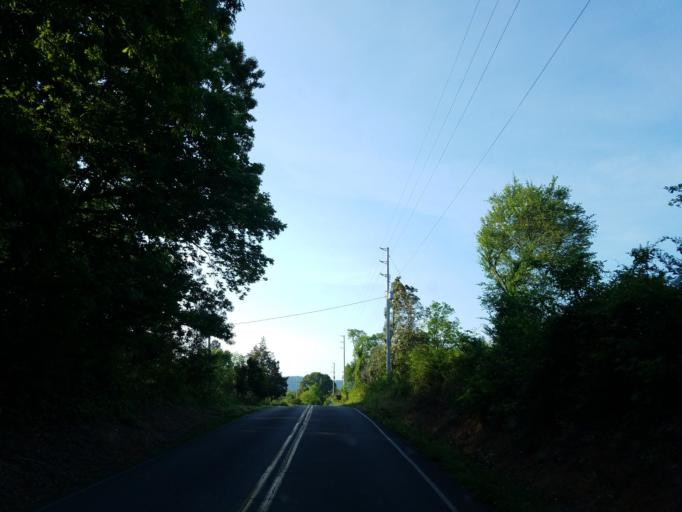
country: US
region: Georgia
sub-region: Gordon County
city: Calhoun
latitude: 34.5026
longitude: -85.1157
